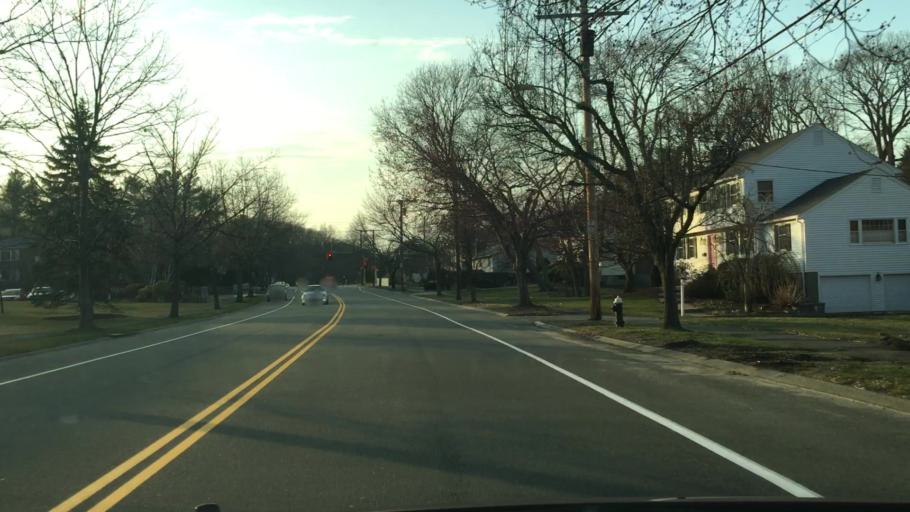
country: US
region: Massachusetts
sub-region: Middlesex County
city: Lexington
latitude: 42.4398
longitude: -71.2310
